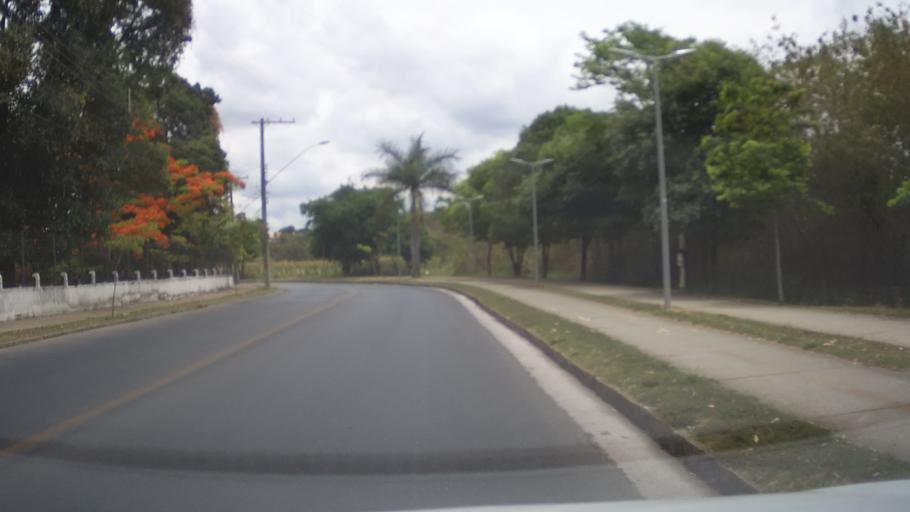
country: BR
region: Minas Gerais
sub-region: Belo Horizonte
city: Belo Horizonte
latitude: -19.8522
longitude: -44.0017
